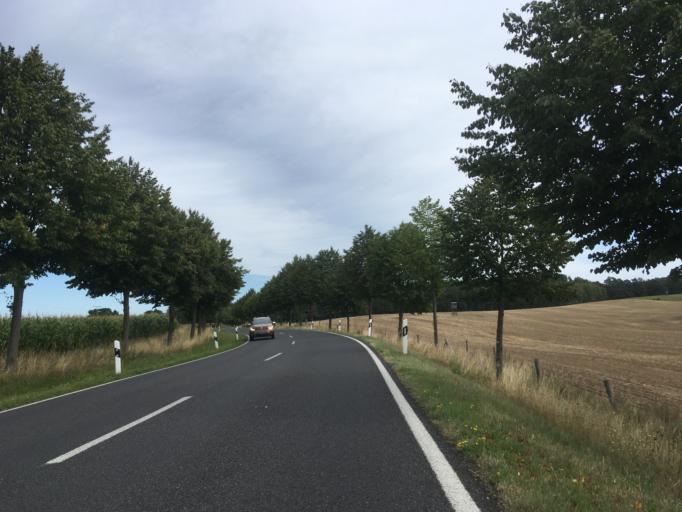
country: DE
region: Brandenburg
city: Templin
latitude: 53.1573
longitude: 13.5574
